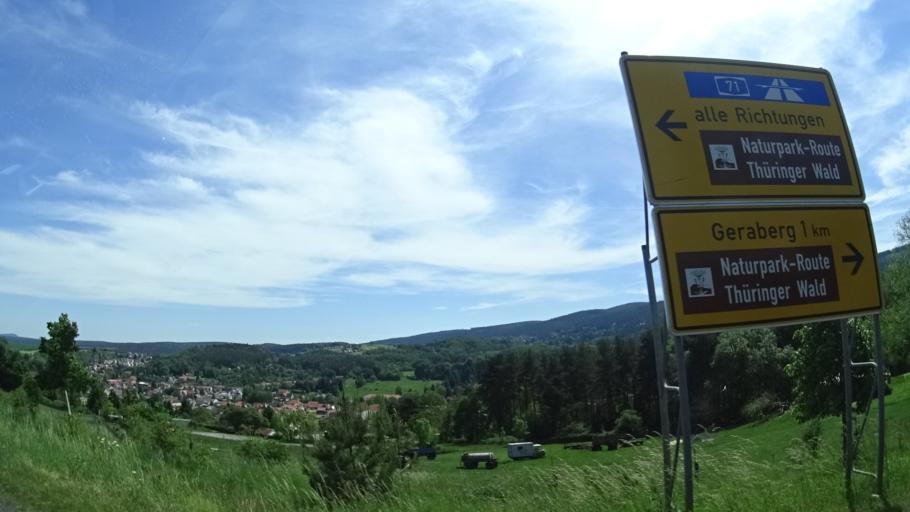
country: DE
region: Thuringia
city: Geraberg
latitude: 50.7191
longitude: 10.8318
